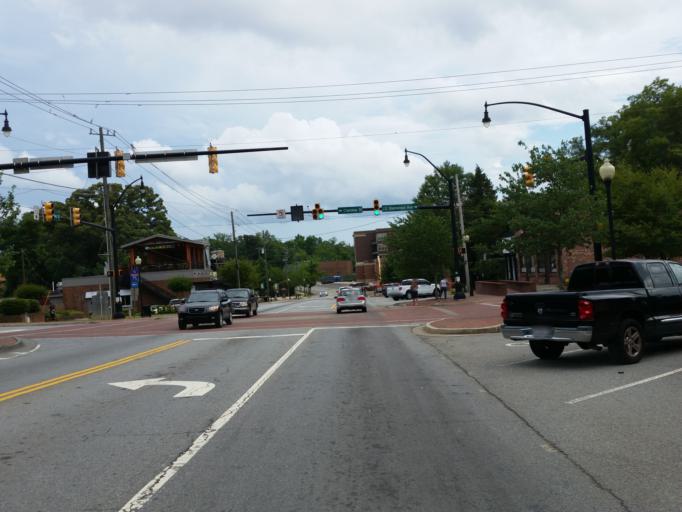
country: US
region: Georgia
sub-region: Cobb County
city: Kennesaw
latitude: 34.0238
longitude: -84.6153
